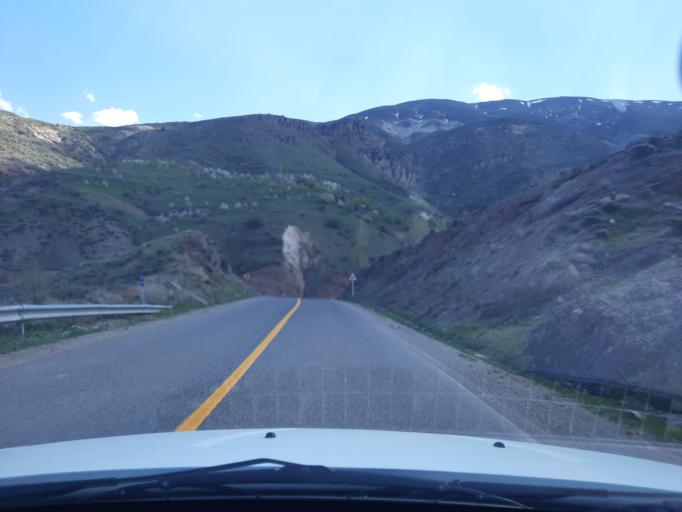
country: IR
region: Qazvin
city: Qazvin
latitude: 36.4058
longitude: 50.2265
